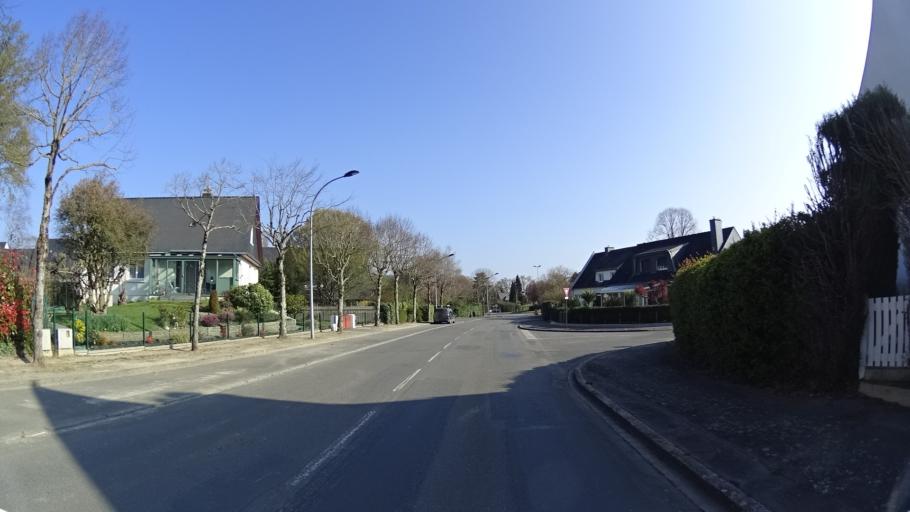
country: FR
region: Brittany
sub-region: Departement d'Ille-et-Vilaine
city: Pace
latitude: 48.1497
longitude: -1.7803
